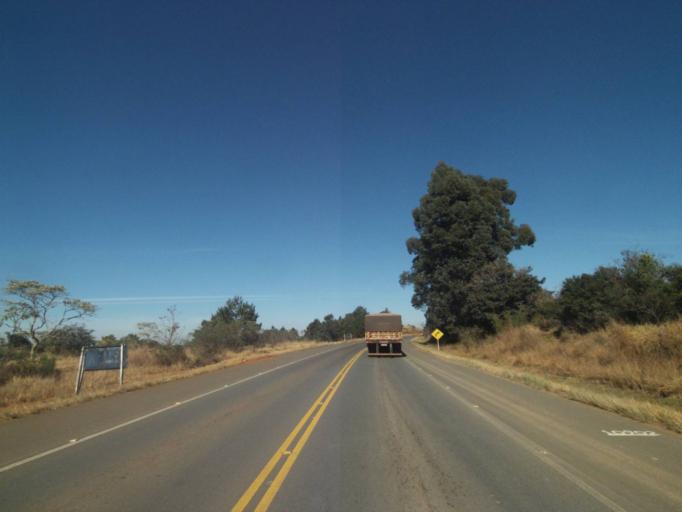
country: BR
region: Parana
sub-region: Tibagi
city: Tibagi
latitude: -24.5997
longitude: -50.4378
